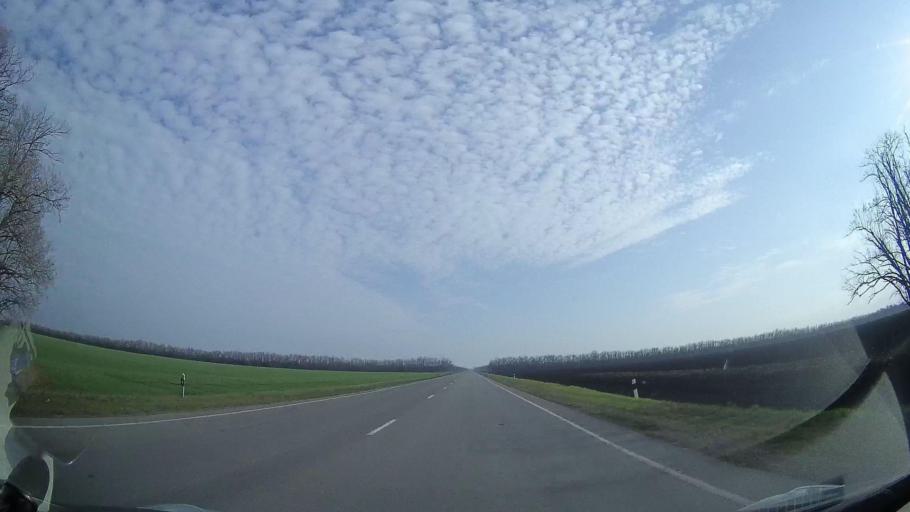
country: RU
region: Rostov
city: Tselina
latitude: 46.5254
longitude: 41.0958
